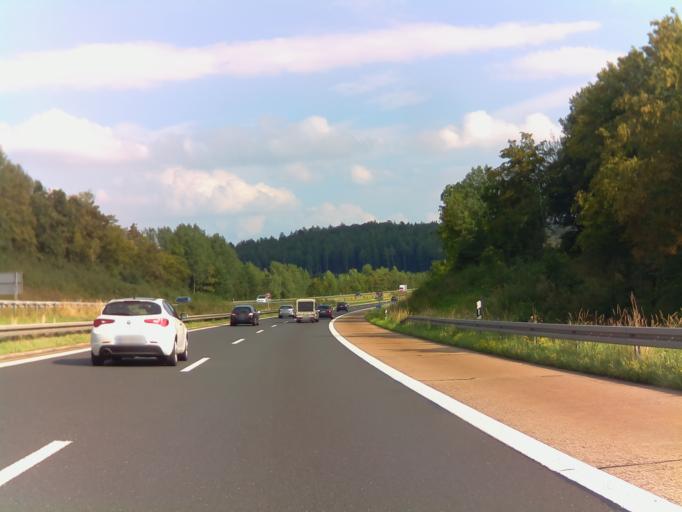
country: DE
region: Bavaria
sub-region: Regierungsbezirk Unterfranken
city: Schondra
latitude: 50.2790
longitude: 9.8695
